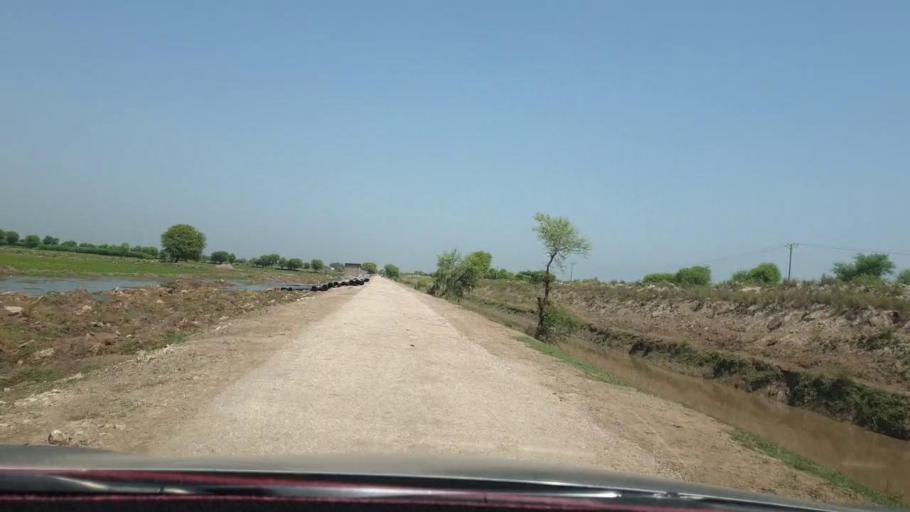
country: PK
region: Sindh
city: Warah
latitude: 27.5093
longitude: 67.7958
